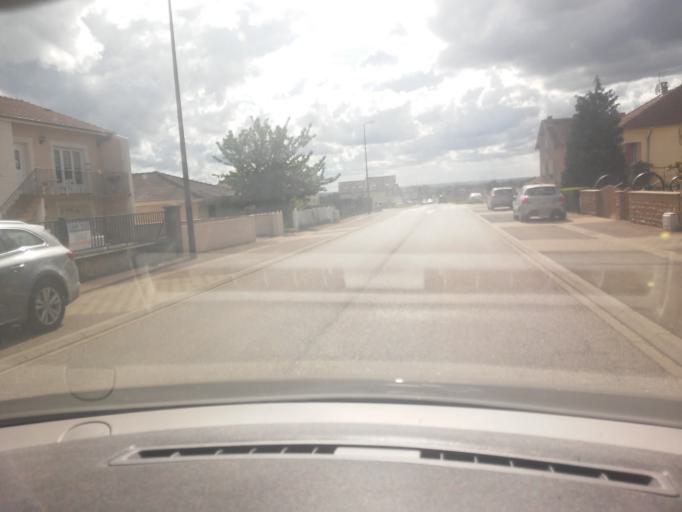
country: FR
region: Lorraine
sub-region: Departement de Meurthe-et-Moselle
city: Labry
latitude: 49.1711
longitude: 5.8720
